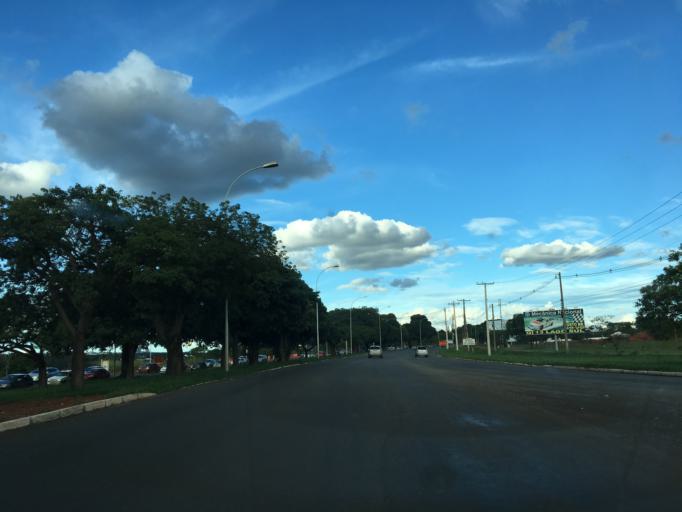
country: BR
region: Federal District
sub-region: Brasilia
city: Brasilia
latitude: -15.8603
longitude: -47.9333
